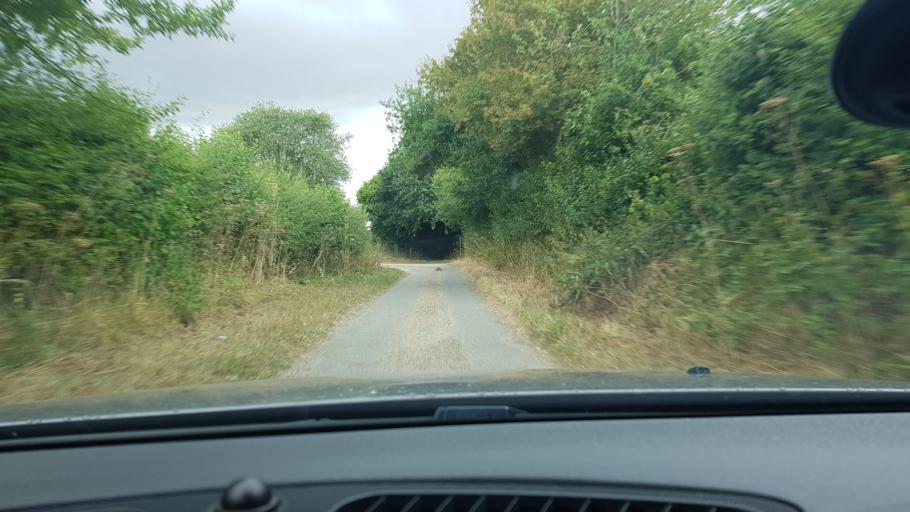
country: GB
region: England
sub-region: West Berkshire
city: Wickham
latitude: 51.4354
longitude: -1.4428
